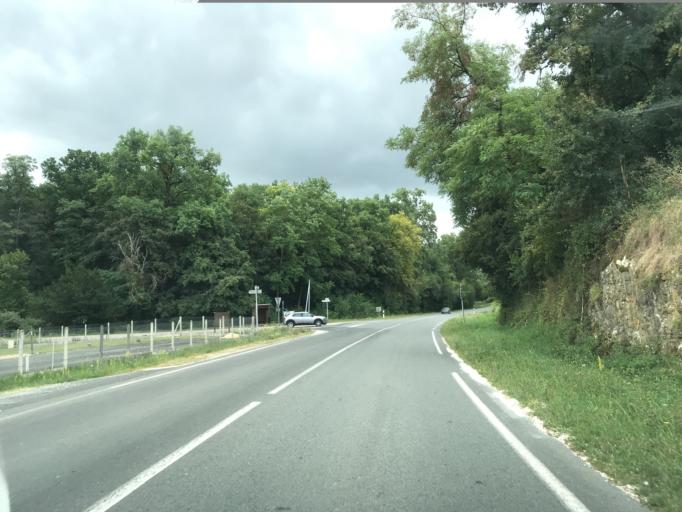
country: FR
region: Aquitaine
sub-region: Departement de la Dordogne
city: Brantome
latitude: 45.3763
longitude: 0.6448
